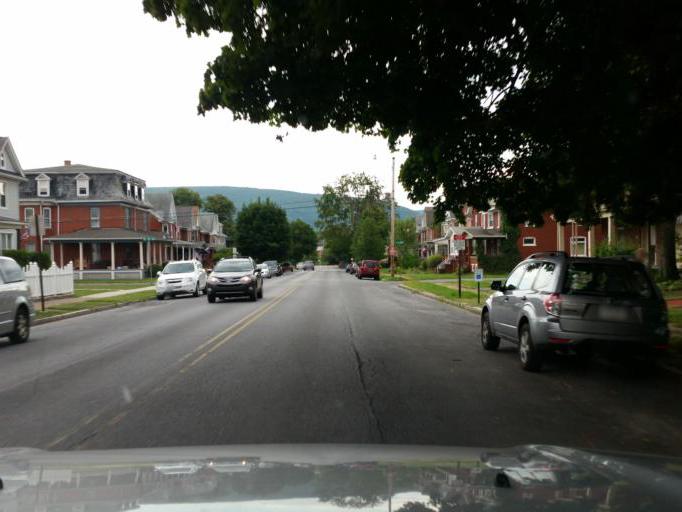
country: US
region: Pennsylvania
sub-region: Blair County
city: Altoona
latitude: 40.5349
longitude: -78.3919
